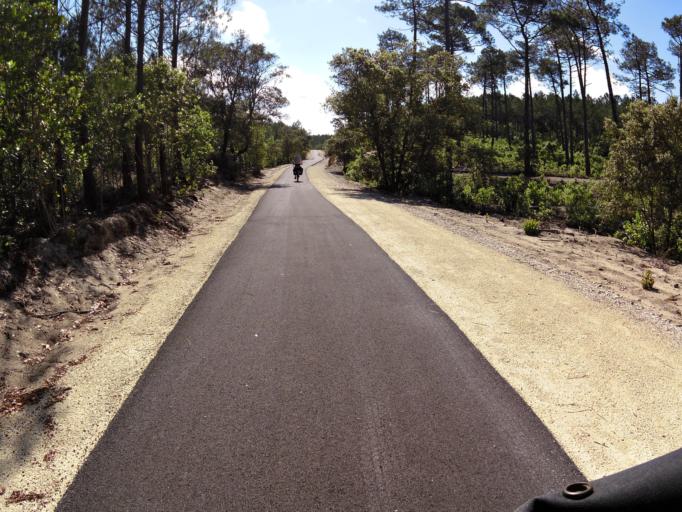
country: FR
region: Aquitaine
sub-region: Departement de la Gironde
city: Lacanau
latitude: 45.0296
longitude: -1.1743
